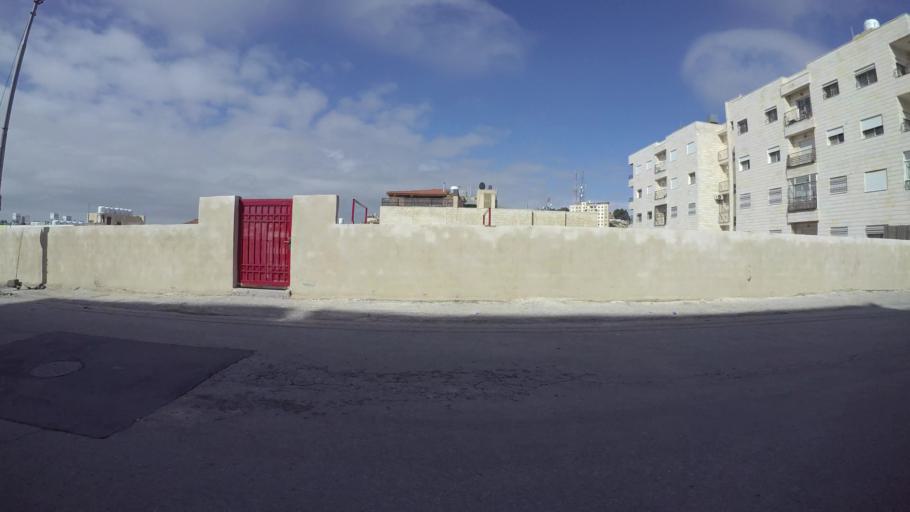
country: JO
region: Amman
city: Al Jubayhah
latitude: 32.0045
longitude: 35.8488
